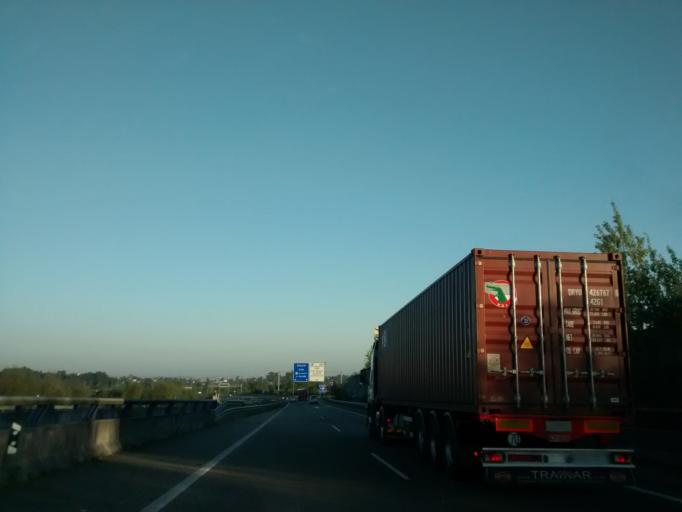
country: ES
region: Asturias
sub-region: Province of Asturias
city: Arriba
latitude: 43.5104
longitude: -5.5621
